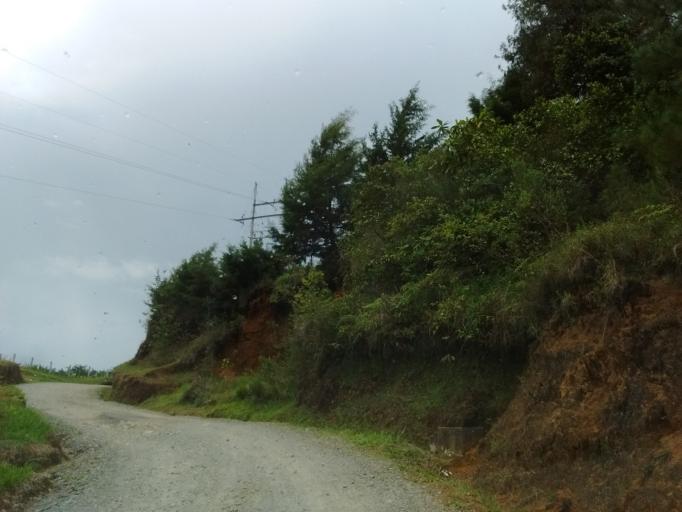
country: CO
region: Cauca
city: Cajibio
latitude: 2.5518
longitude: -76.6274
